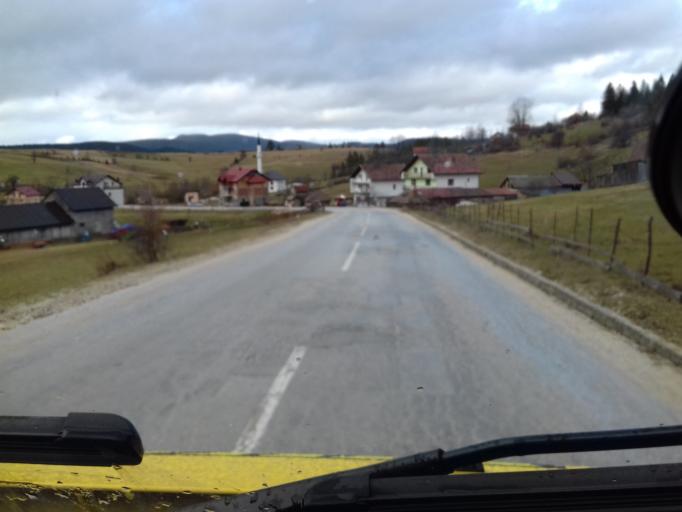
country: BA
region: Federation of Bosnia and Herzegovina
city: Turbe
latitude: 44.3144
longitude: 17.5292
